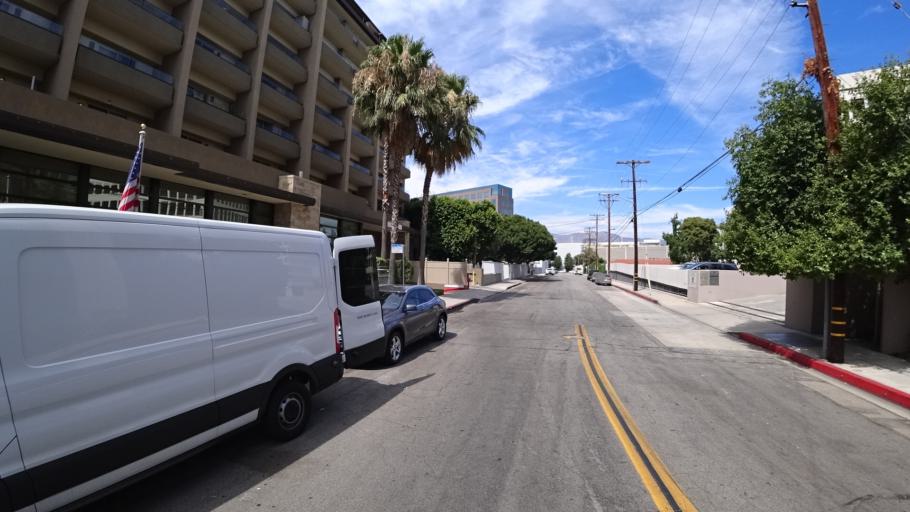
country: US
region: California
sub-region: Los Angeles County
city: Universal City
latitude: 34.1579
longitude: -118.3312
